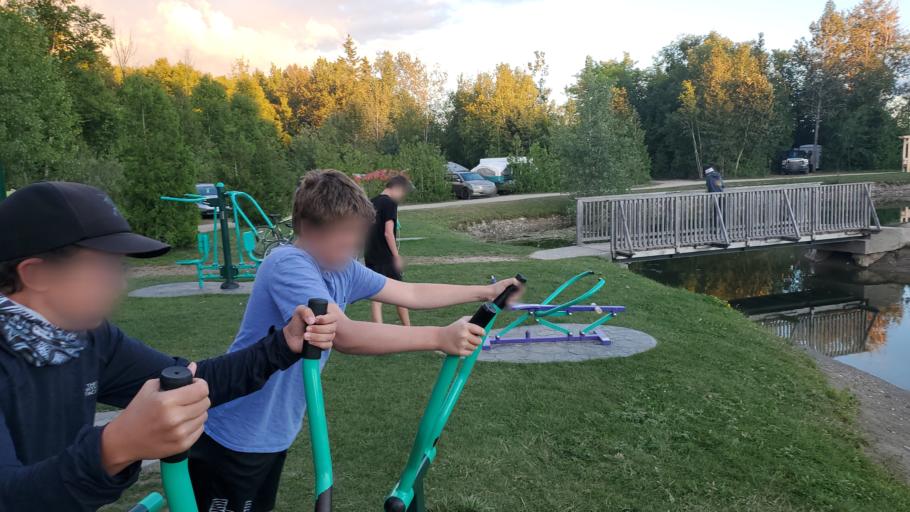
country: CA
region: Ontario
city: Tobermory
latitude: 45.2330
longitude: -81.6426
